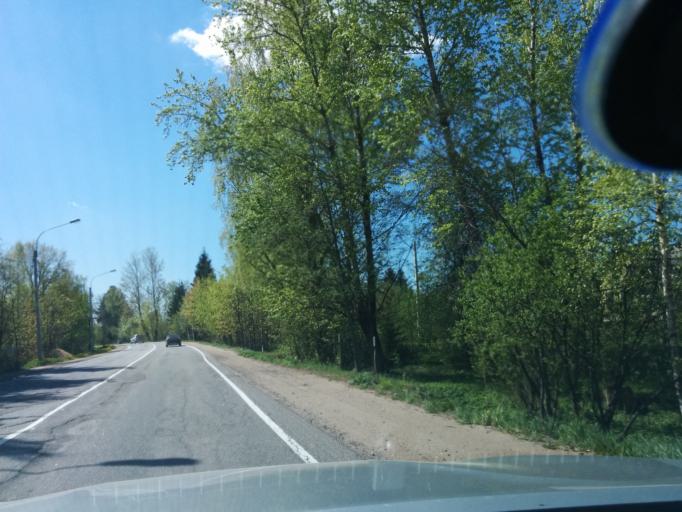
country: RU
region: Leningrad
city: Verkhniye Osel'ki
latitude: 60.2540
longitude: 30.4501
